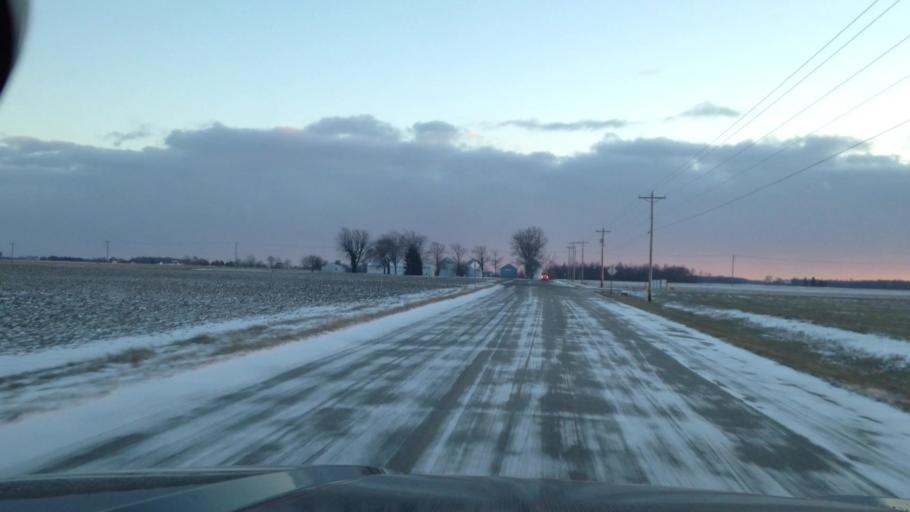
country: US
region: Indiana
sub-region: Randolph County
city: Union City
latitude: 40.1814
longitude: -84.8624
